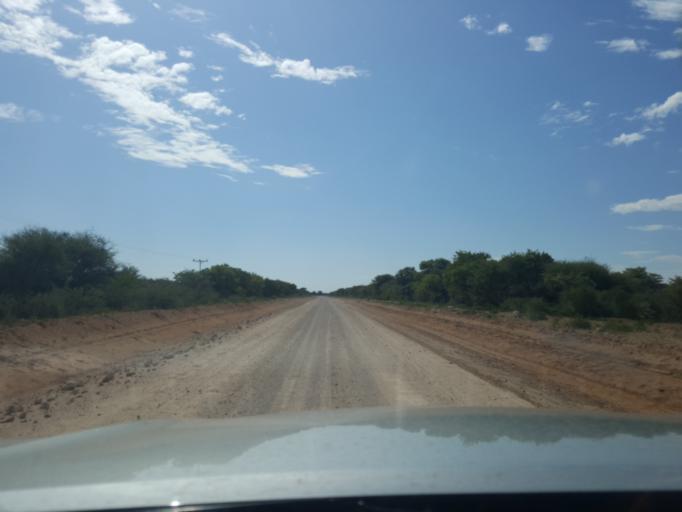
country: BW
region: Kweneng
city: Khudumelapye
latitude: -23.7970
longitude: 24.7978
